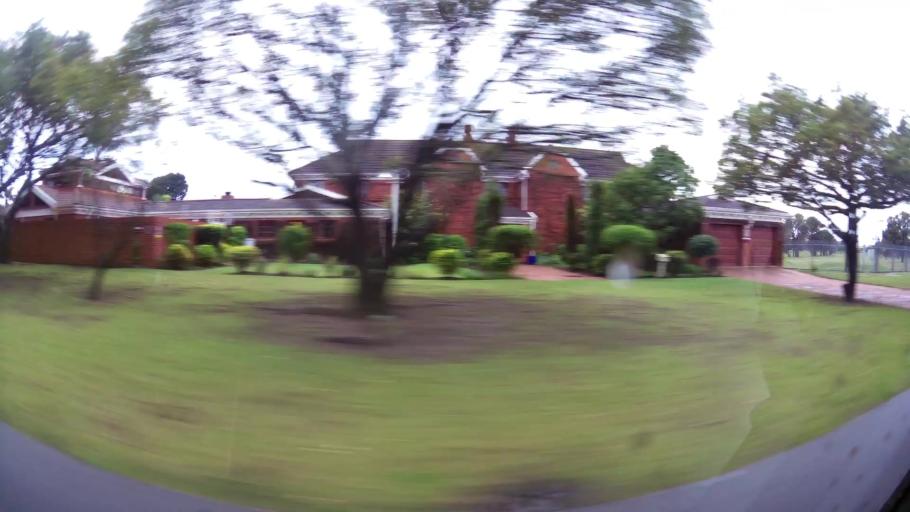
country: ZA
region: Eastern Cape
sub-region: Nelson Mandela Bay Metropolitan Municipality
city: Port Elizabeth
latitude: -33.9777
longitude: 25.5688
